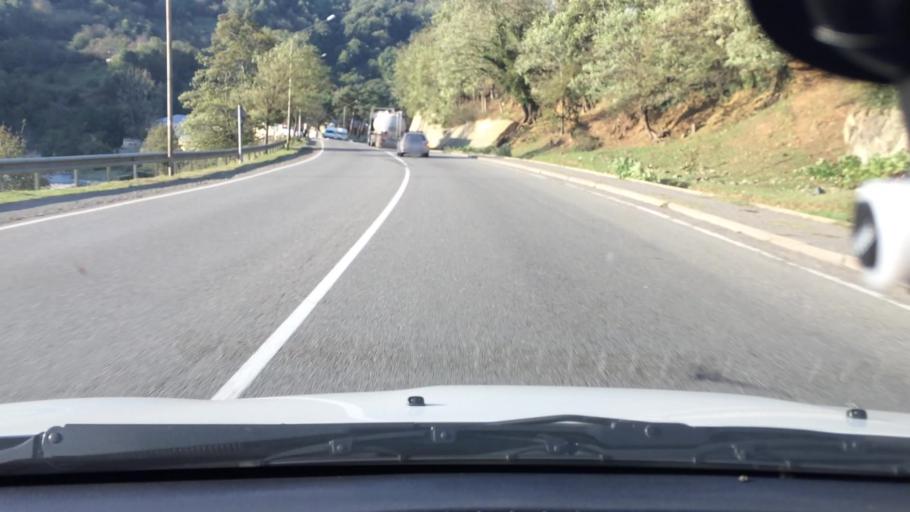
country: GE
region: Imereti
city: Kharagauli
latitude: 42.1112
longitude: 43.2698
